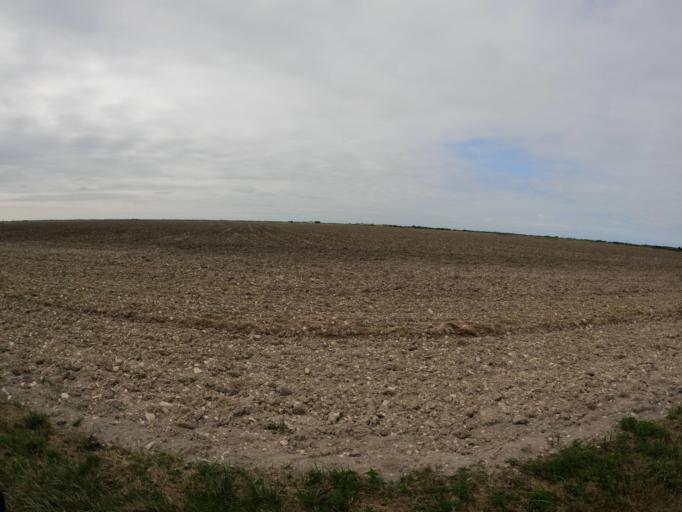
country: FR
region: Poitou-Charentes
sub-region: Departement de la Charente-Maritime
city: Charron
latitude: 46.3059
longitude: -1.0566
